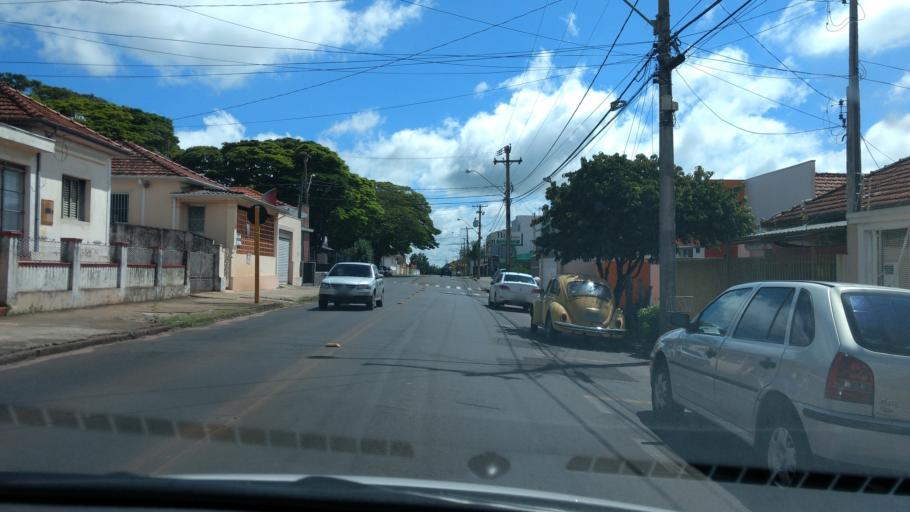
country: BR
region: Sao Paulo
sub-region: Botucatu
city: Botucatu
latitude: -22.8702
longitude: -48.4448
